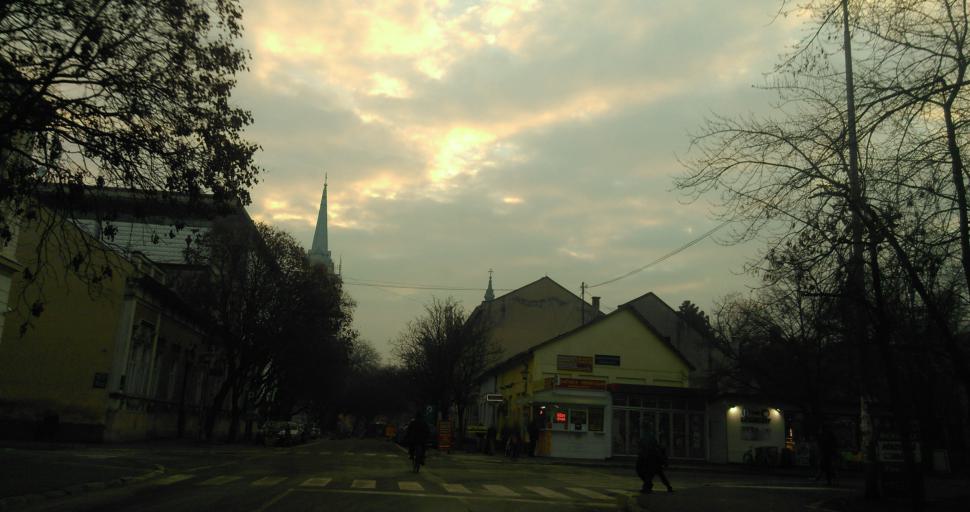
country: RS
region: Autonomna Pokrajina Vojvodina
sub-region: Juznobacki Okrug
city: Becej
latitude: 45.6166
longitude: 20.0473
